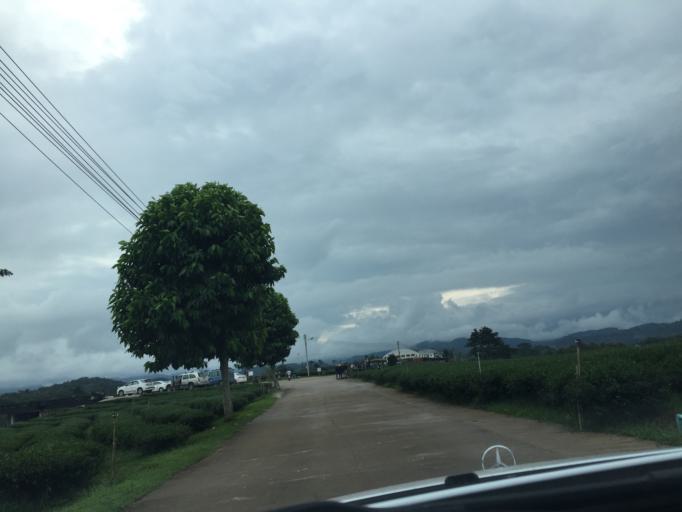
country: TH
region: Chiang Rai
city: Mae Chan
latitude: 20.2014
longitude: 99.8211
